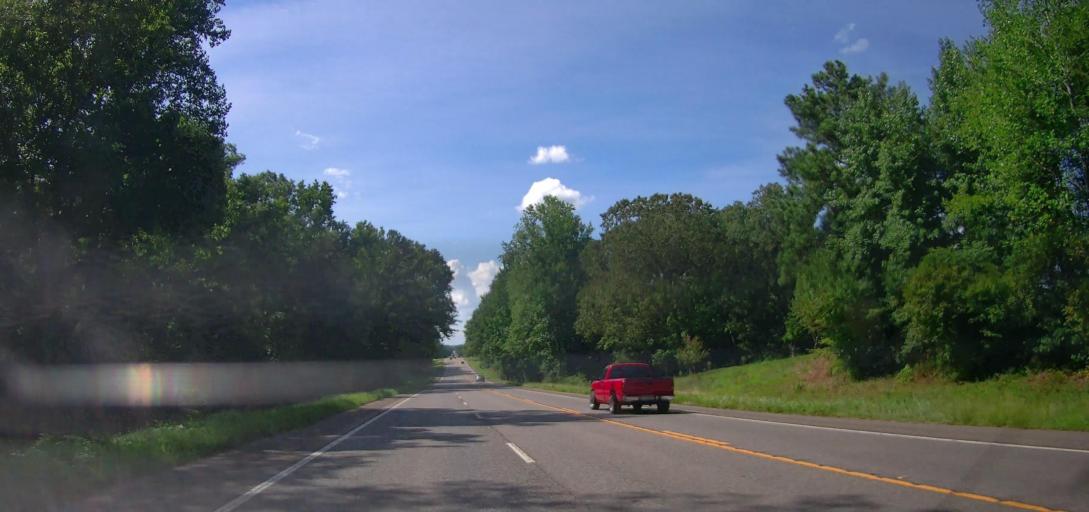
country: US
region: Alabama
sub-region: Pickens County
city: Gordo
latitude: 33.2921
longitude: -87.8723
